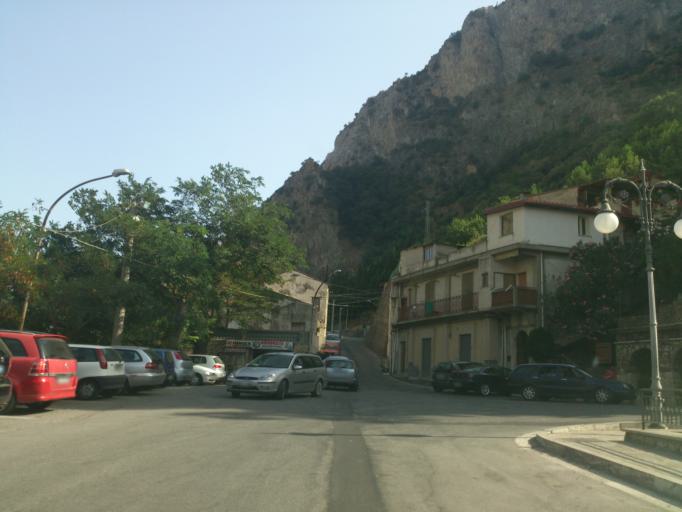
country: IT
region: Calabria
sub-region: Provincia di Reggio Calabria
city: Pazzano
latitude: 38.4747
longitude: 16.4529
